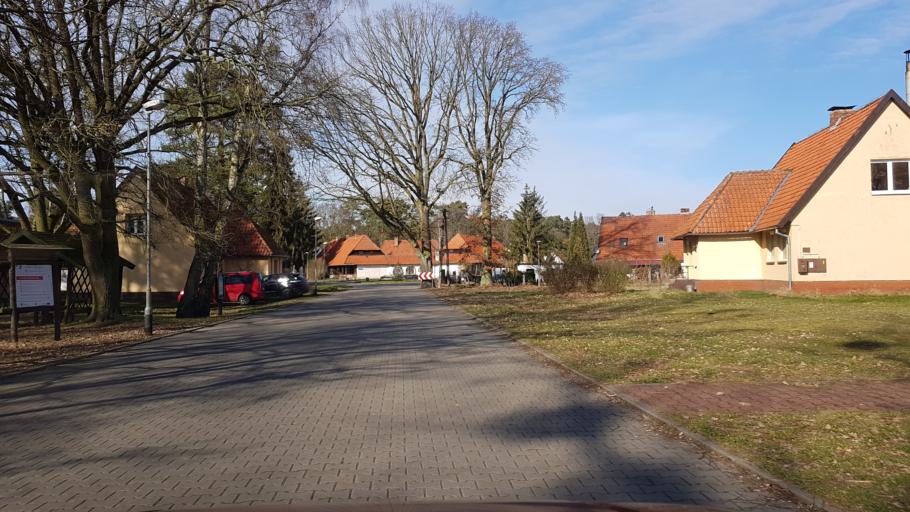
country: PL
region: West Pomeranian Voivodeship
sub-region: Powiat policki
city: Nowe Warpno
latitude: 53.7341
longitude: 14.3088
